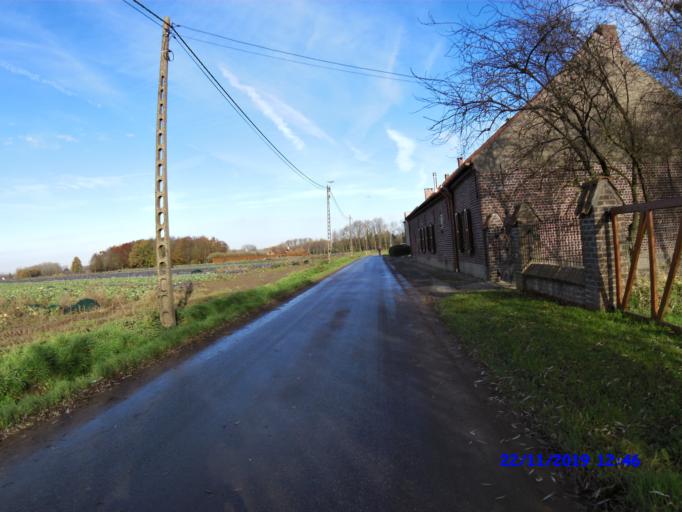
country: BE
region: Flanders
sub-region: Provincie Vlaams-Brabant
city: Merchtem
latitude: 50.9644
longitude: 4.2682
